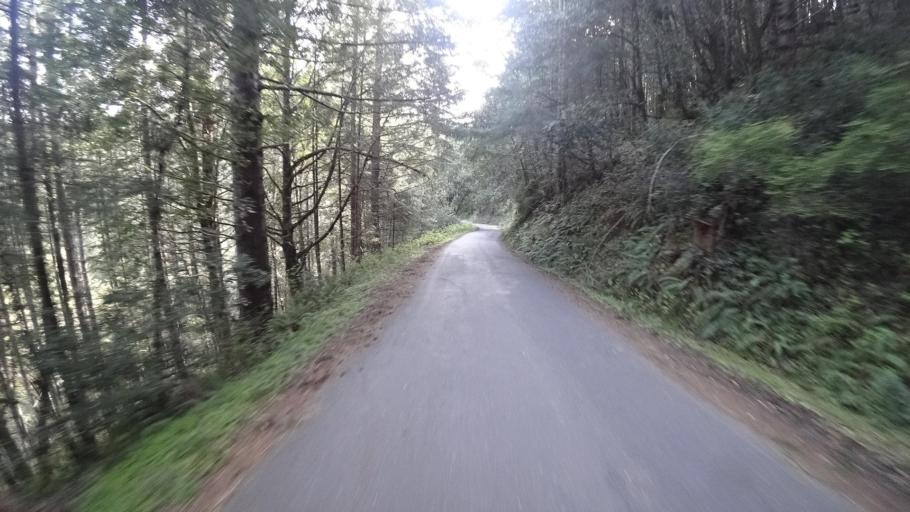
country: US
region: California
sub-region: Humboldt County
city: Bayside
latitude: 40.6954
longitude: -123.9417
